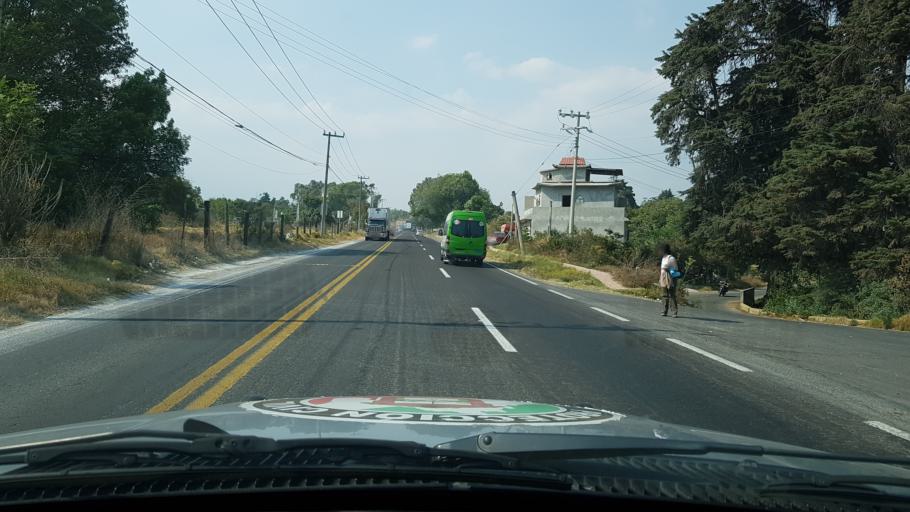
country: MX
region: Mexico
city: Tepetlixpa
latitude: 19.0175
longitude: -98.8245
